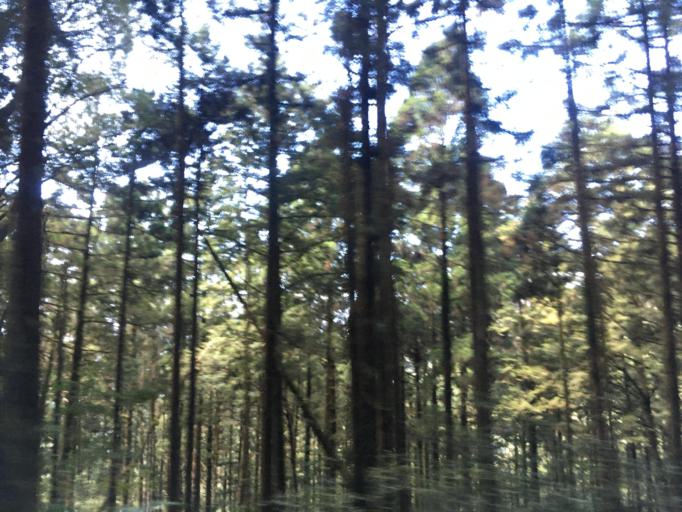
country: TW
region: Taiwan
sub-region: Yilan
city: Yilan
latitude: 24.6170
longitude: 121.4816
